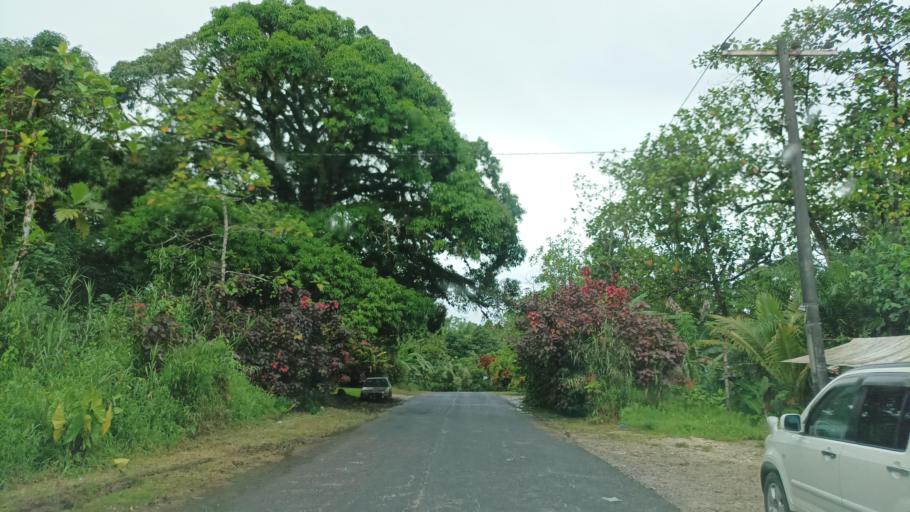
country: FM
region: Pohnpei
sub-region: Sokehs Municipality
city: Palikir - National Government Center
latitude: 6.8448
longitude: 158.1578
